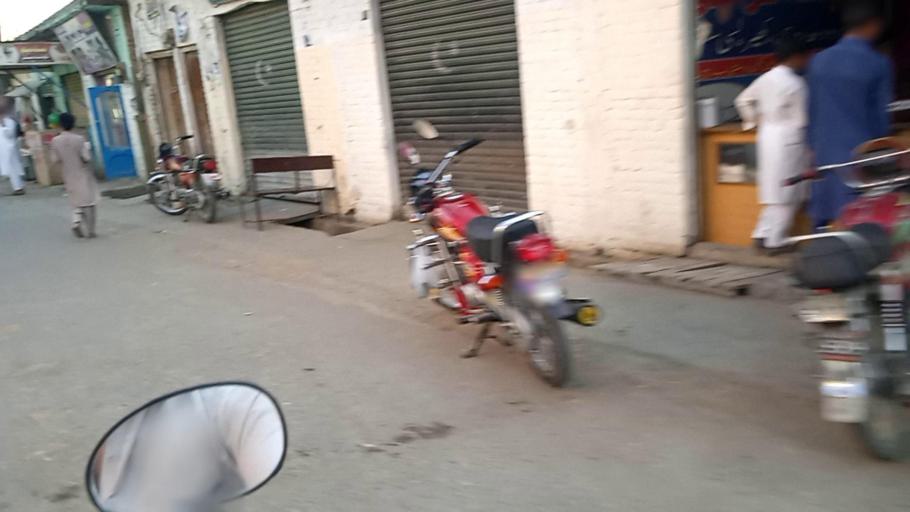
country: PK
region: Khyber Pakhtunkhwa
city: Mingora
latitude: 34.8143
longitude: 72.3590
